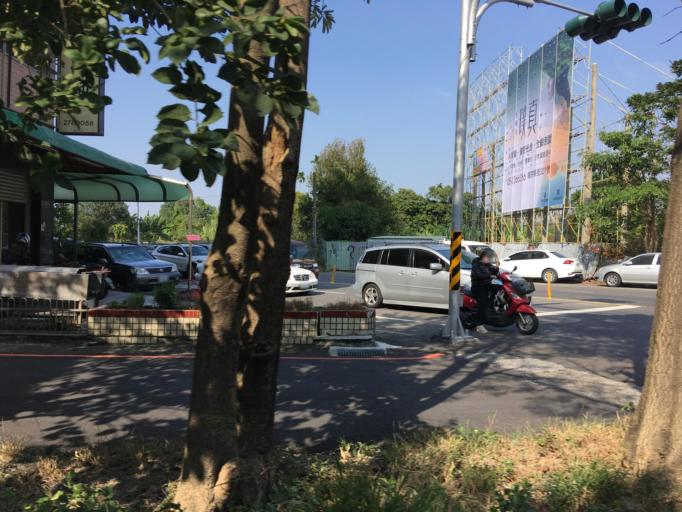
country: TW
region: Taiwan
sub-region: Chiayi
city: Jiayi Shi
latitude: 23.4899
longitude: 120.4629
